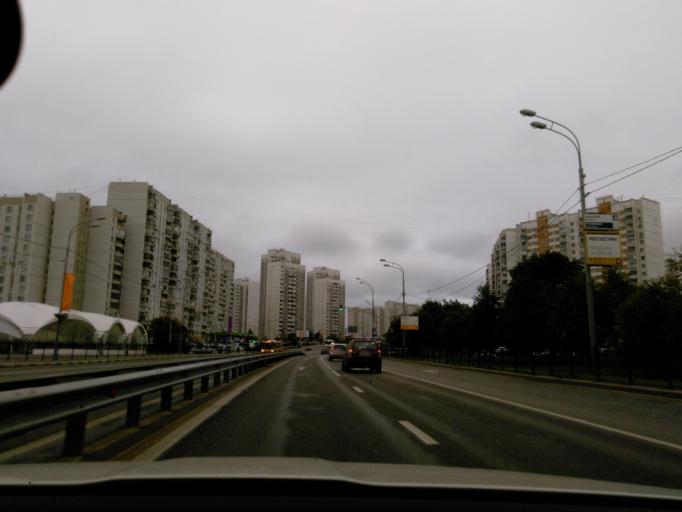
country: RU
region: Moscow
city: Strogino
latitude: 55.8432
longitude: 37.3818
